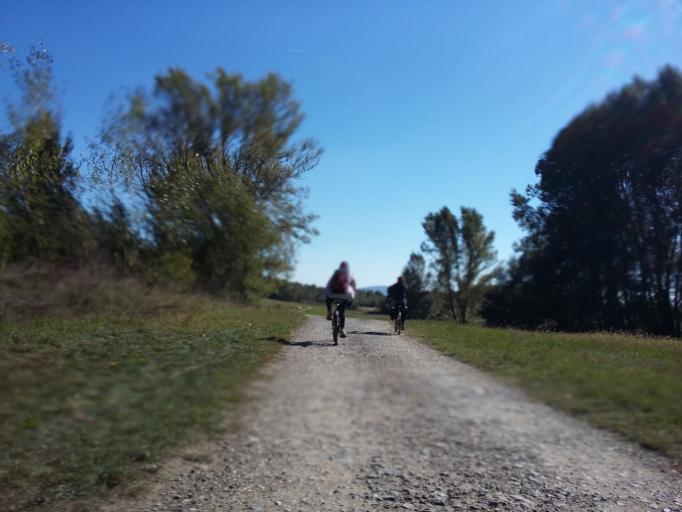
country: AT
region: Lower Austria
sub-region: Politischer Bezirk Ganserndorf
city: Marchegg
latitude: 48.3163
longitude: 16.9122
